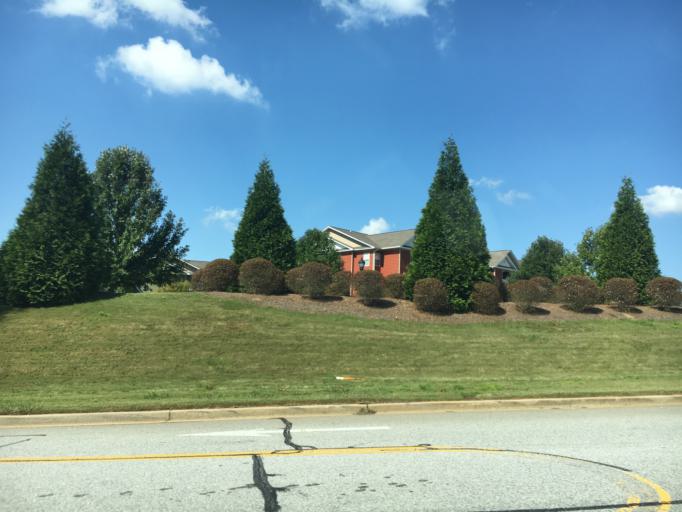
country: US
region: South Carolina
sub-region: Spartanburg County
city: Wellford
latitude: 34.8970
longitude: -82.0745
